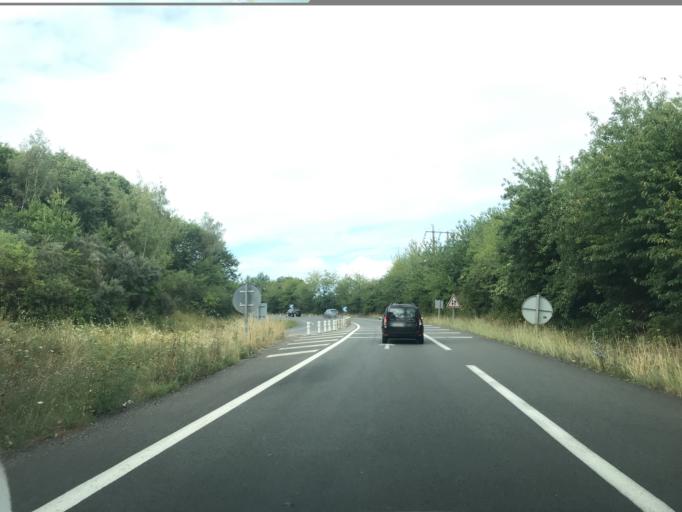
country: FR
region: Poitou-Charentes
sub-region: Departement de la Vienne
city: Vouneuil-sous-Biard
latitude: 46.5557
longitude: 0.2828
